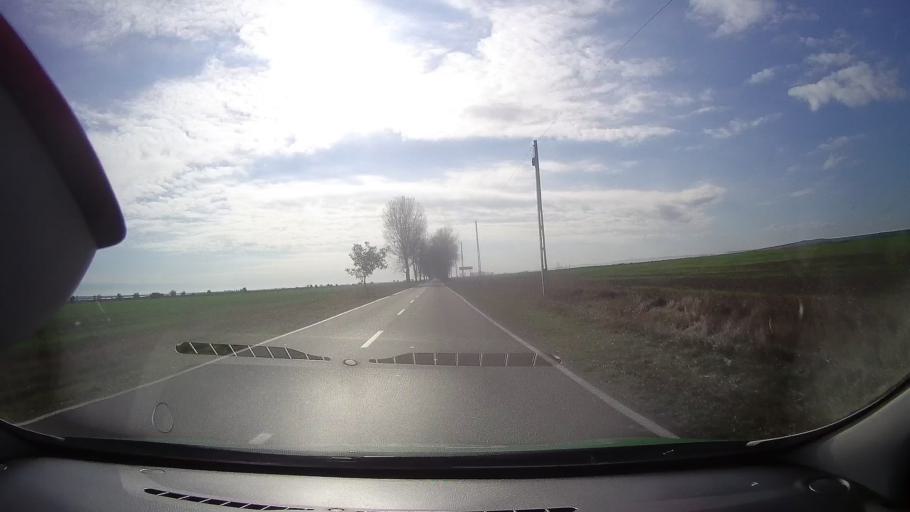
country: RO
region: Tulcea
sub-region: Comuna Valea Nucarilor
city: Agighiol
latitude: 45.0140
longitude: 28.8838
